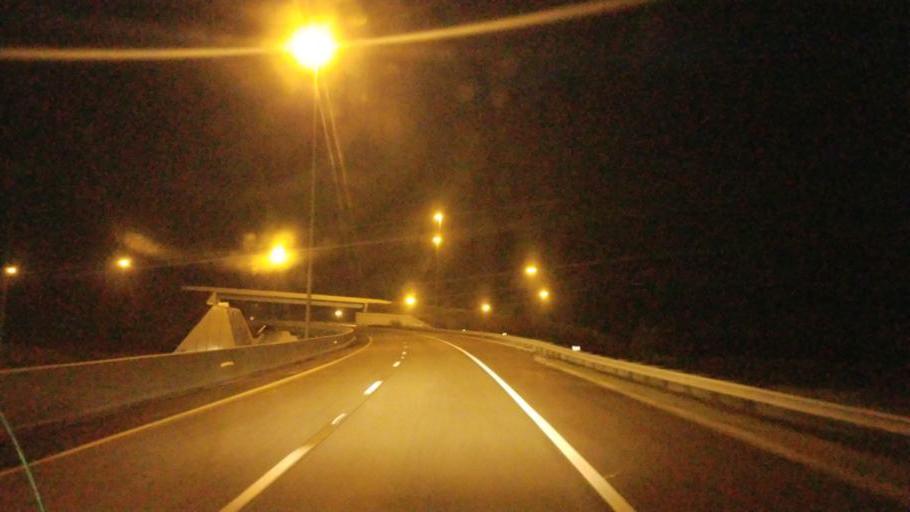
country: US
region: Ohio
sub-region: Wyandot County
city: Upper Sandusky
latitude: 40.8139
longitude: -83.2369
